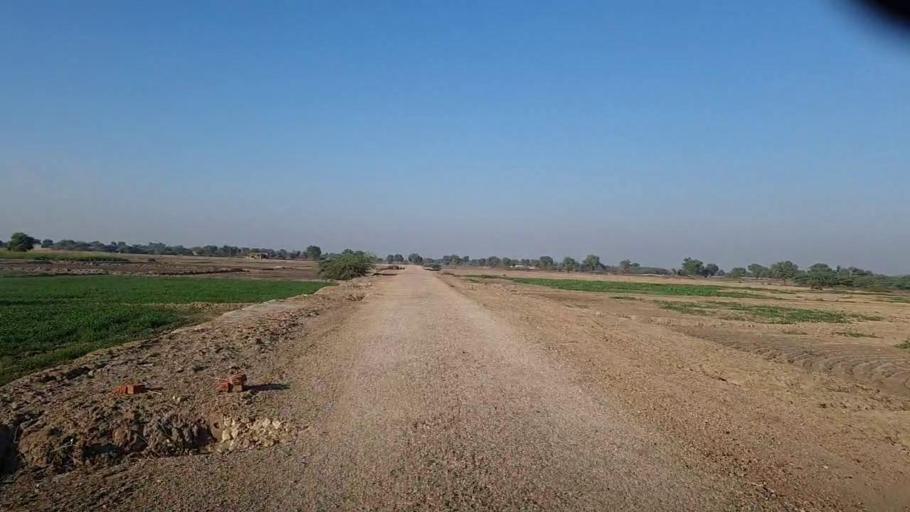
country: PK
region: Sindh
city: Pad Idan
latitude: 26.7313
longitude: 68.3492
